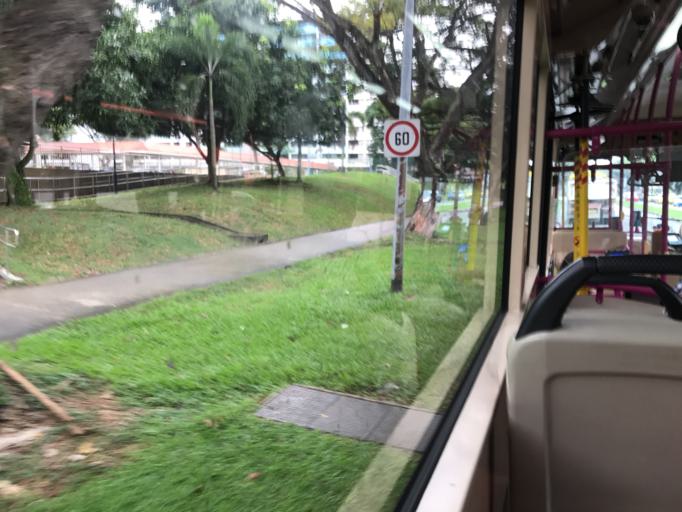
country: SG
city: Singapore
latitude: 1.3294
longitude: 103.9267
